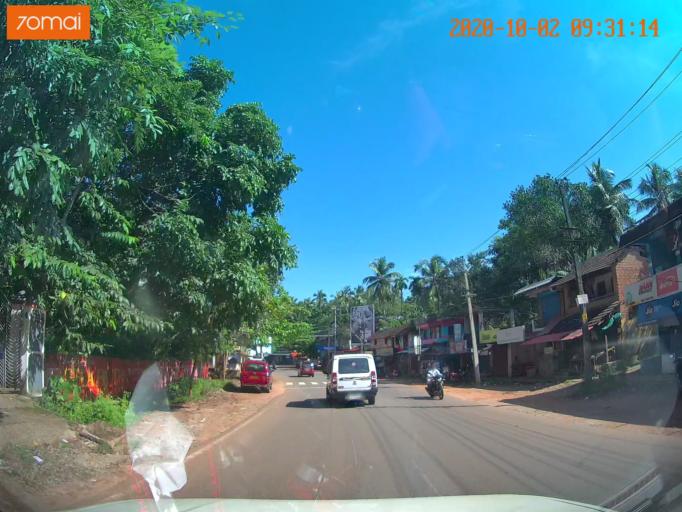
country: IN
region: Kerala
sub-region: Kozhikode
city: Nadapuram
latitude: 11.6230
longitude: 75.7612
